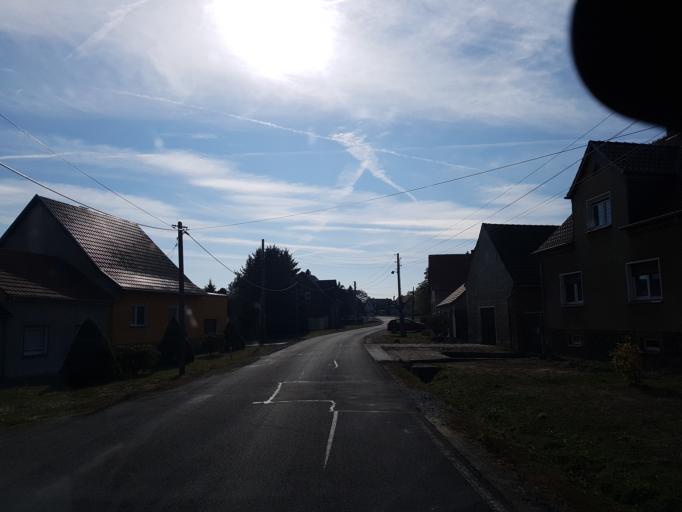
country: DE
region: Brandenburg
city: Schonborn
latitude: 51.6689
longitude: 13.4725
